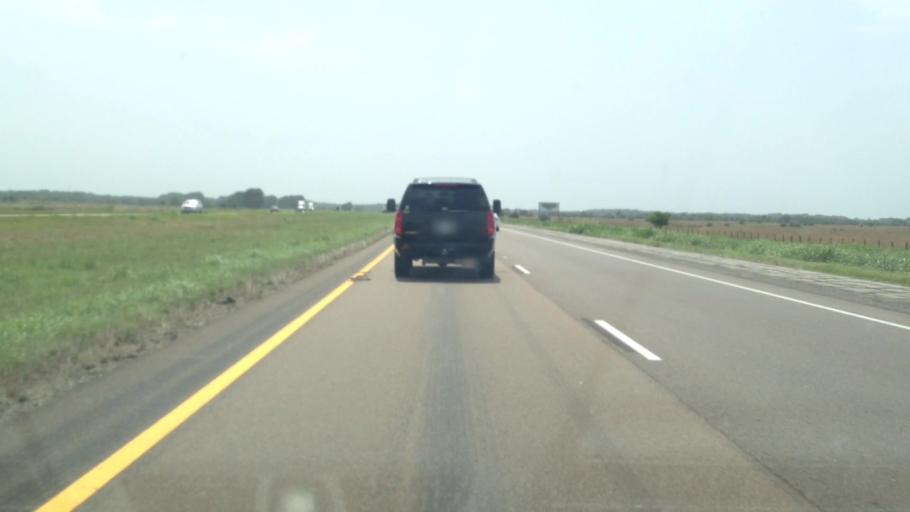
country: US
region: Texas
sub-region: Morris County
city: Omaha
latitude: 33.2901
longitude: -94.7771
